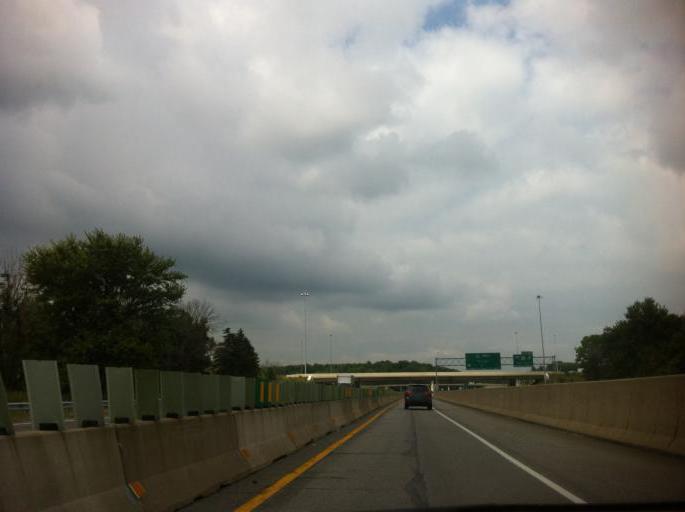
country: US
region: Ohio
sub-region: Cuyahoga County
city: Strongsville
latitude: 41.3318
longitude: -81.8136
